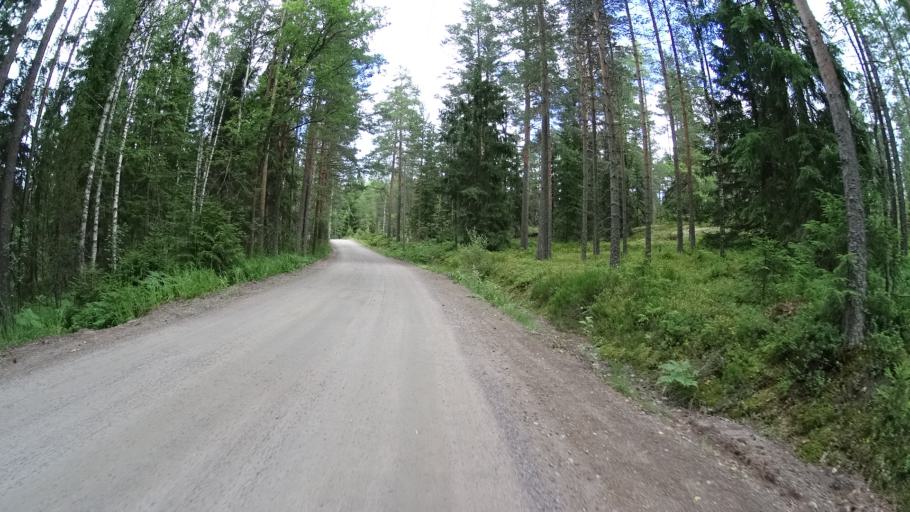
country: FI
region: Uusimaa
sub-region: Helsinki
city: Espoo
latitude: 60.2905
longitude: 24.6120
